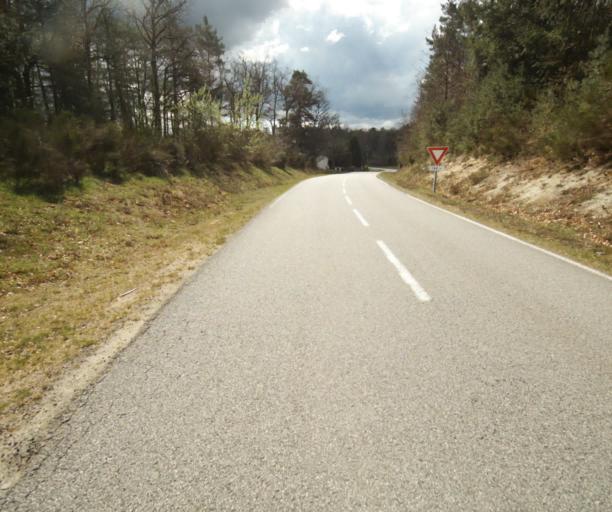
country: FR
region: Limousin
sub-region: Departement de la Correze
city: Correze
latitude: 45.2915
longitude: 1.8979
